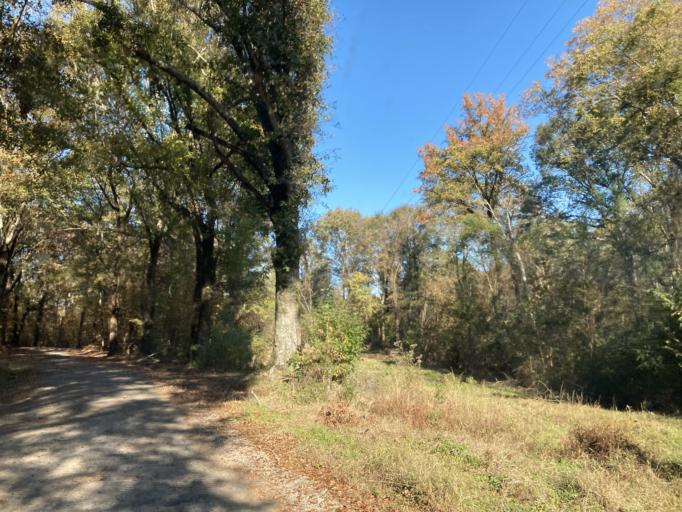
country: US
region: Mississippi
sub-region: Yazoo County
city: Yazoo City
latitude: 32.7609
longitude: -90.2785
